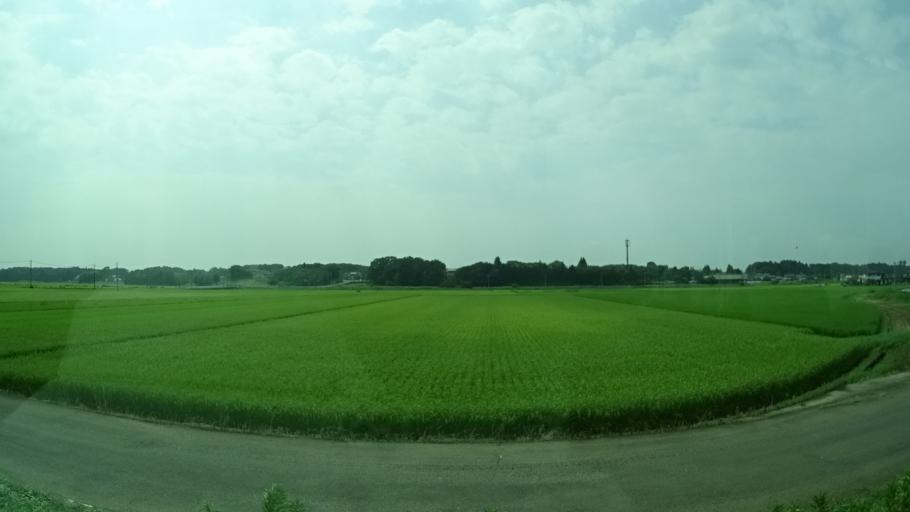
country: JP
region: Tochigi
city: Mashiko
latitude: 36.4901
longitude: 140.0942
